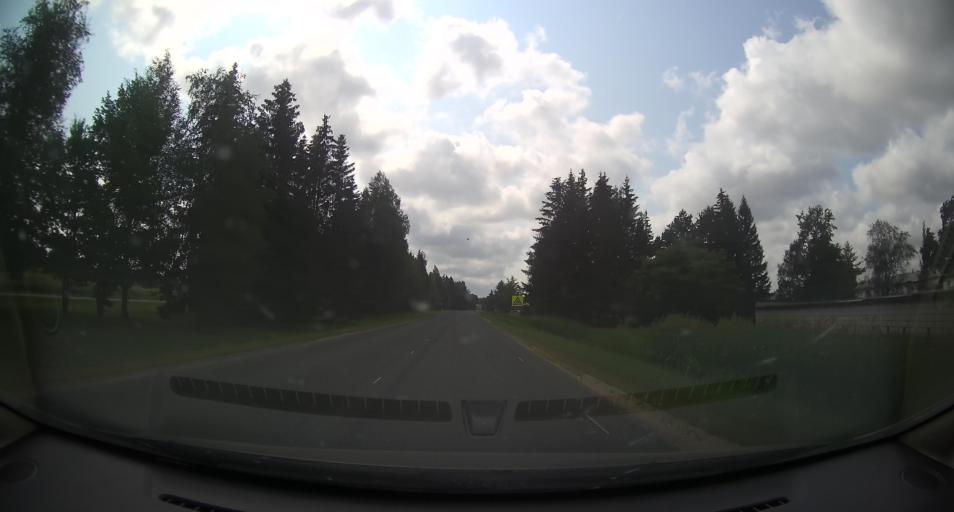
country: EE
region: Paernumaa
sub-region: Audru vald
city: Audru
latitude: 58.4758
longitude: 24.3280
